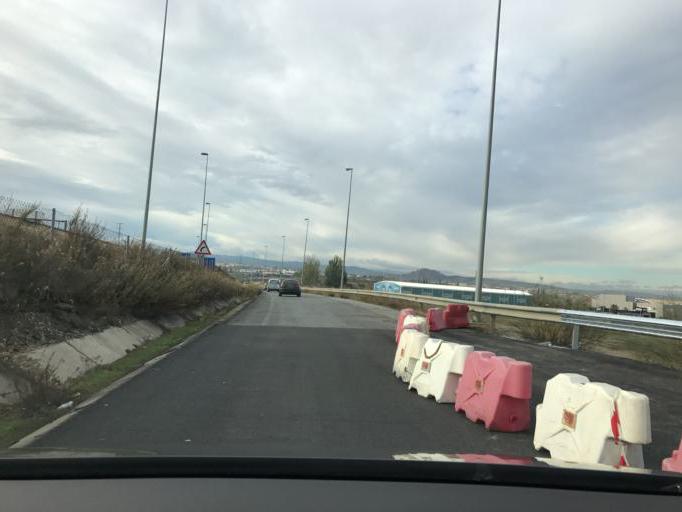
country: ES
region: Andalusia
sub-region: Provincia de Granada
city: Armilla
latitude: 37.1446
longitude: -3.6035
